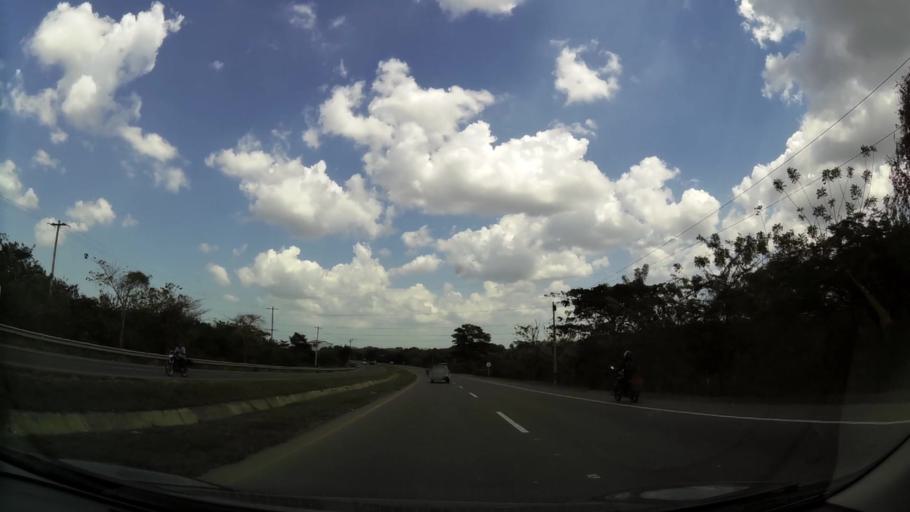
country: CO
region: Bolivar
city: Turbaco
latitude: 10.3645
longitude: -75.4595
